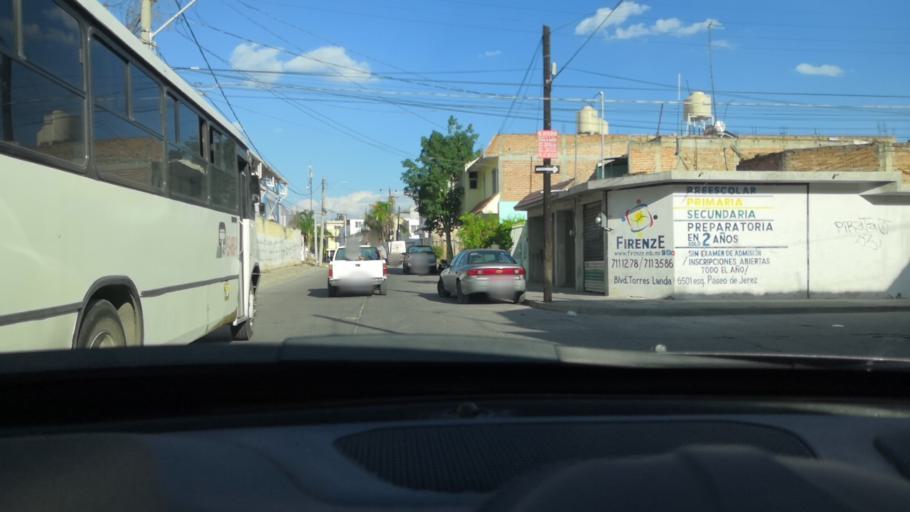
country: MX
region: Guanajuato
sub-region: Leon
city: San Jose de Duran (Los Troncoso)
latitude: 21.0940
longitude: -101.6497
